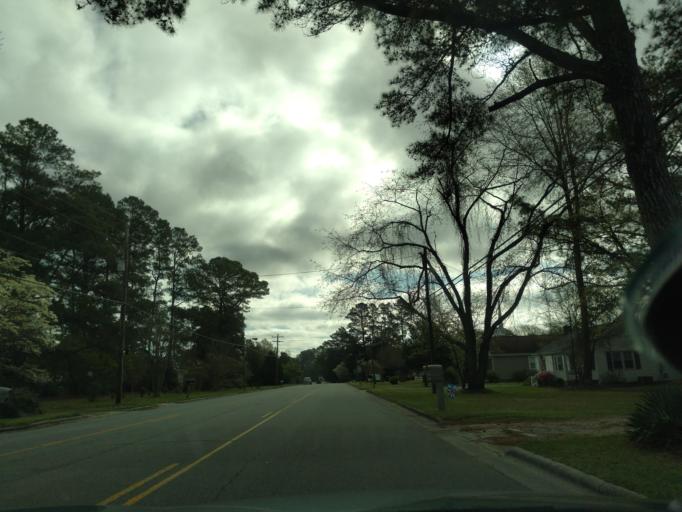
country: US
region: North Carolina
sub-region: Chowan County
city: Edenton
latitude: 36.0567
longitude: -76.6337
